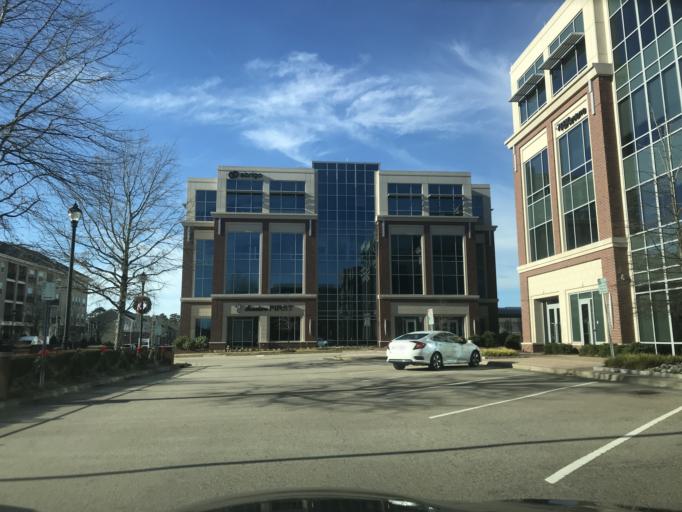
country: US
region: North Carolina
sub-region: Wake County
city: Cary
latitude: 35.8077
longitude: -78.7298
